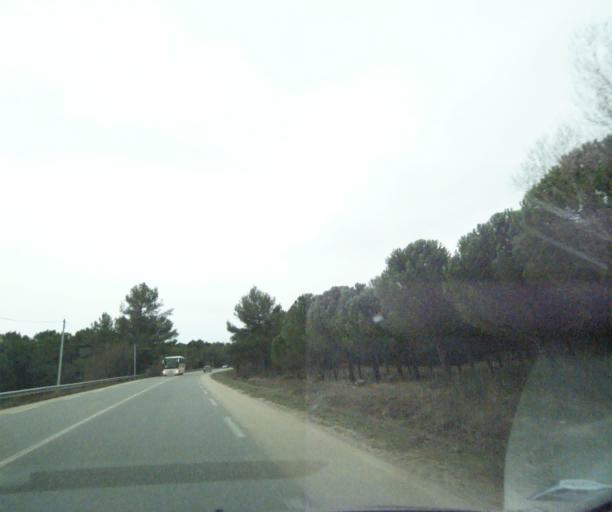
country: FR
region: Provence-Alpes-Cote d'Azur
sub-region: Departement des Bouches-du-Rhone
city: Meyrargues
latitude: 43.6247
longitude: 5.5091
